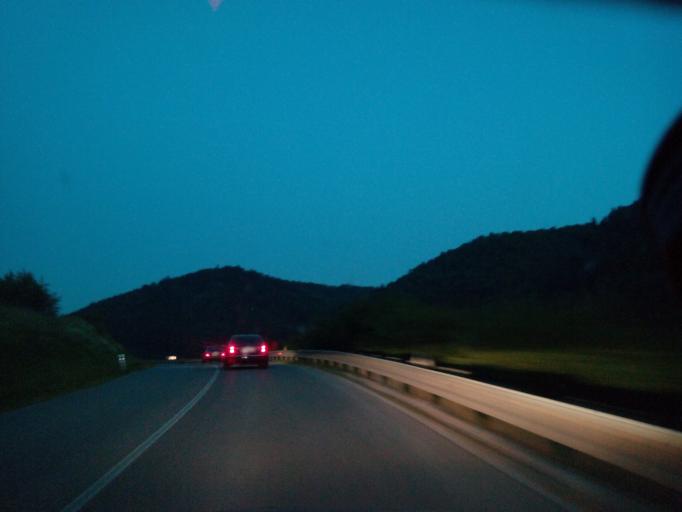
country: SK
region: Kosicky
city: Krompachy
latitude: 48.9308
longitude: 20.8412
